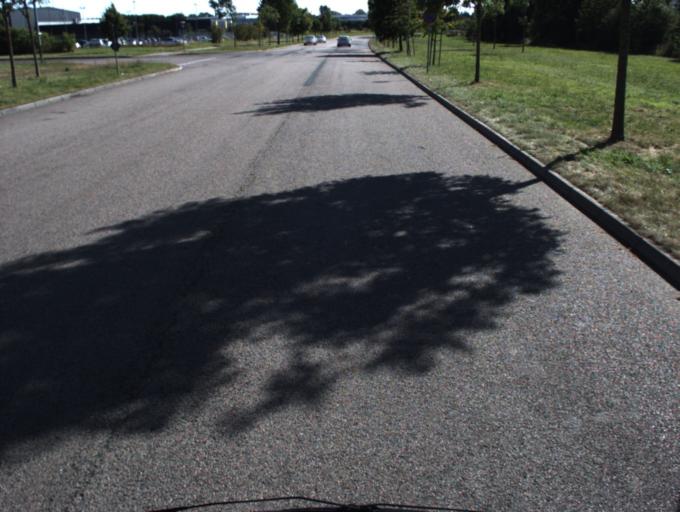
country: SE
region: Skane
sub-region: Helsingborg
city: Odakra
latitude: 56.0776
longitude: 12.7535
